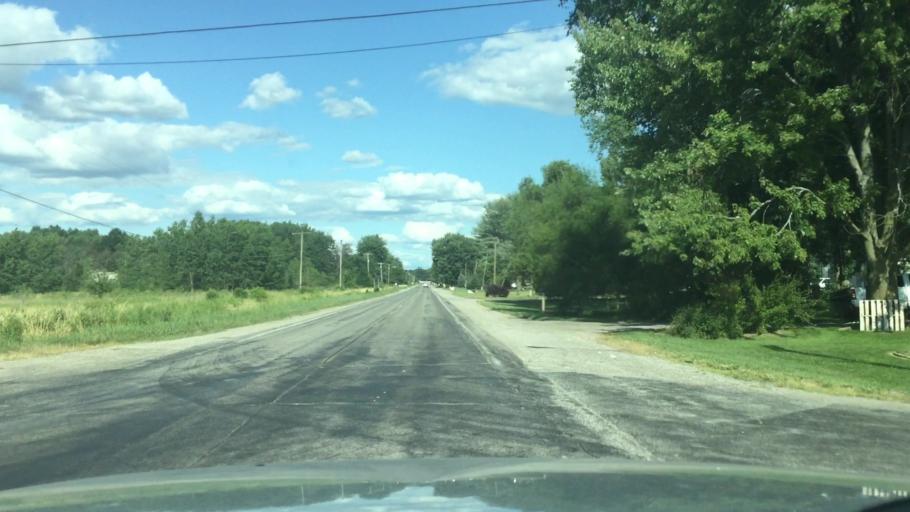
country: US
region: Michigan
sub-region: Saginaw County
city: Shields
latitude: 43.3794
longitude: -84.0719
